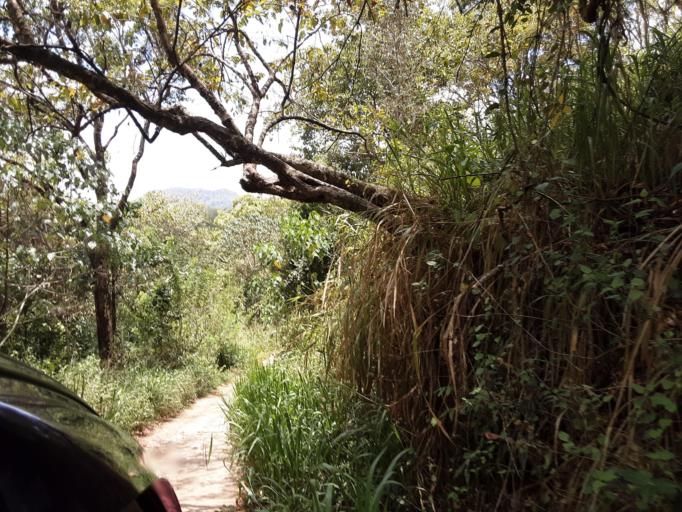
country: LK
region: Uva
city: Haputale
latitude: 6.8131
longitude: 81.1096
